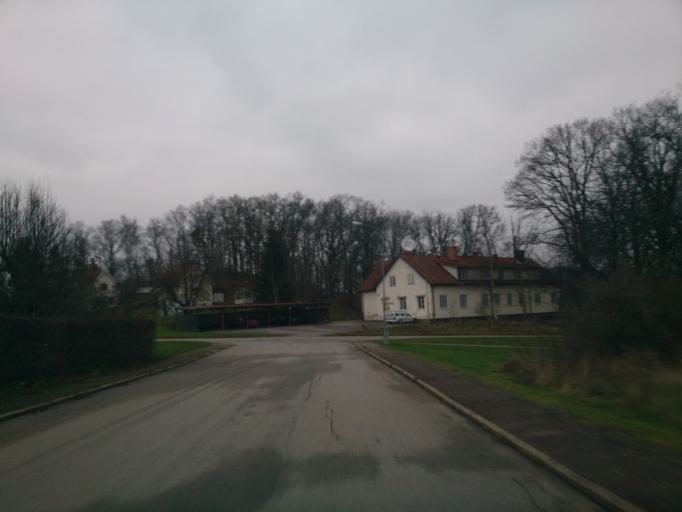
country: SE
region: OEstergoetland
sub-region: Atvidabergs Kommun
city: Atvidaberg
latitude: 58.1958
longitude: 16.0135
